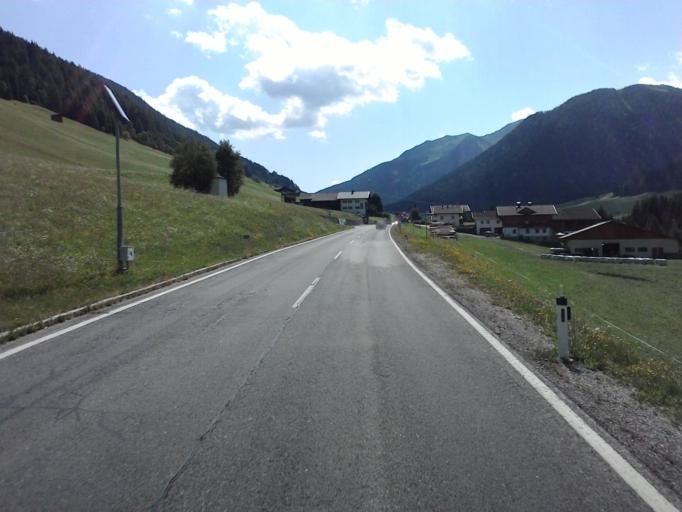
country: AT
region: Tyrol
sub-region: Politischer Bezirk Lienz
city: Kartitsch
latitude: 46.7329
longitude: 12.4843
